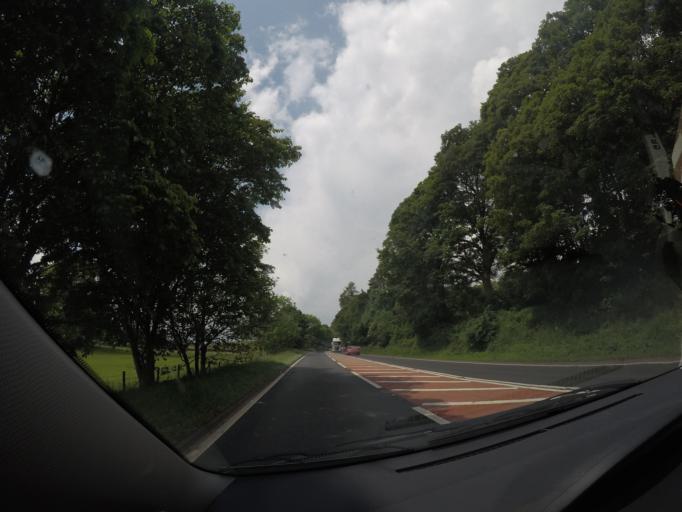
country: GB
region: England
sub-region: Cumbria
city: Kirkby Stephen
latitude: 54.5391
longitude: -2.3857
